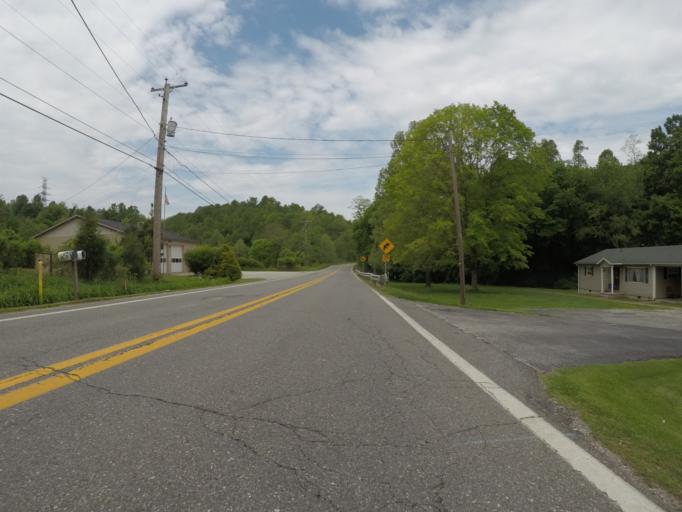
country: US
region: West Virginia
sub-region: Wayne County
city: Ceredo
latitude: 38.3556
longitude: -82.5311
